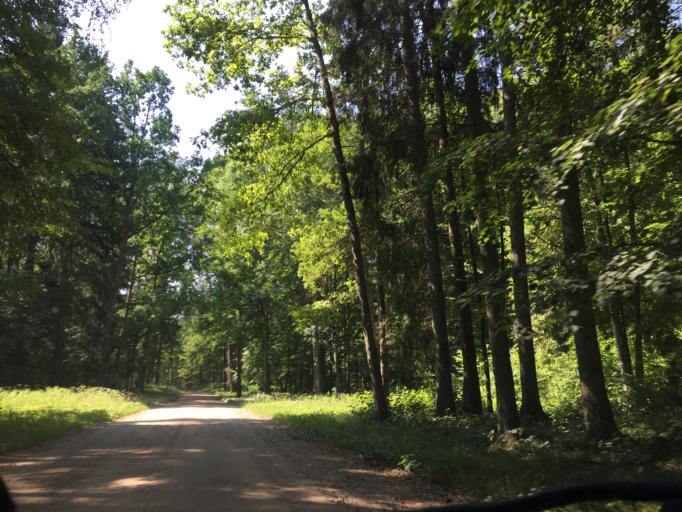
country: LV
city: Tervete
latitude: 56.4840
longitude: 23.3987
